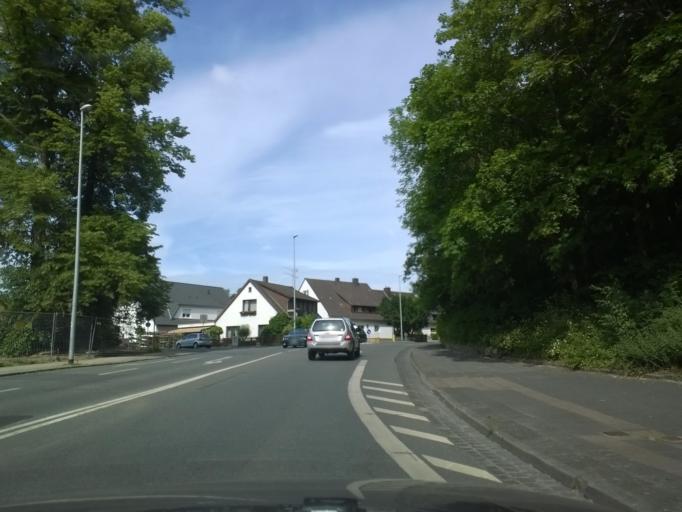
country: DE
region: Lower Saxony
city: Hildesheim
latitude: 52.1405
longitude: 9.9295
